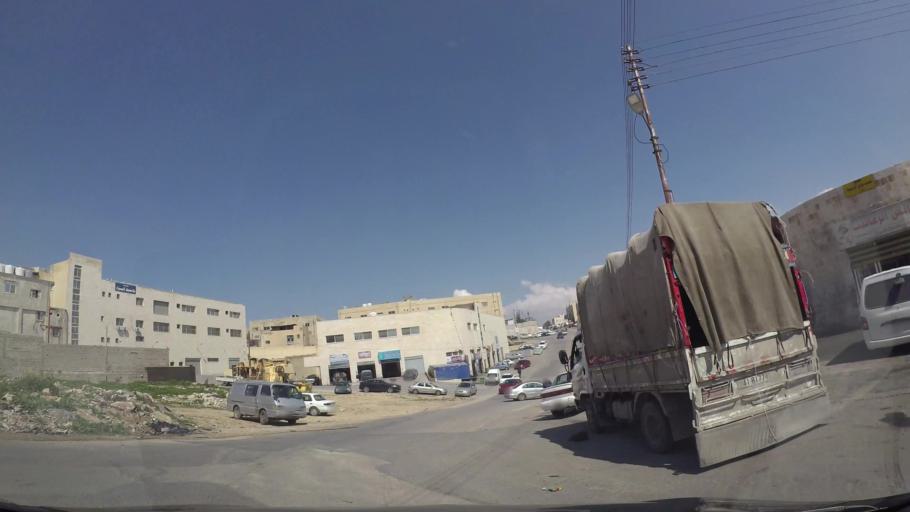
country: JO
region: Zarqa
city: Russeifa
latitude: 31.9883
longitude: 36.0023
